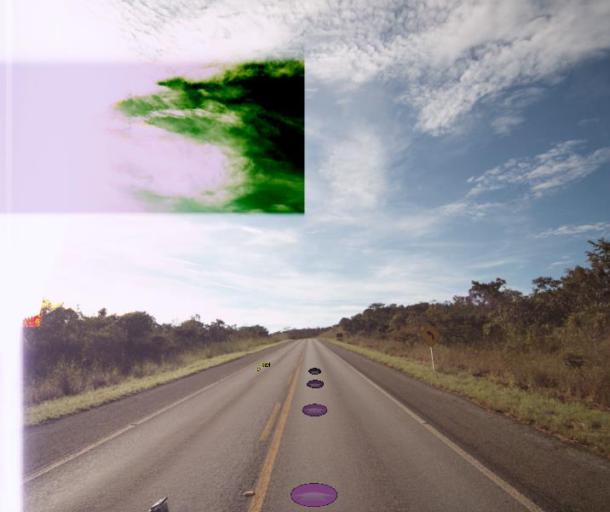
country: BR
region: Goias
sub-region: Pirenopolis
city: Pirenopolis
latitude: -15.7720
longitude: -48.5597
